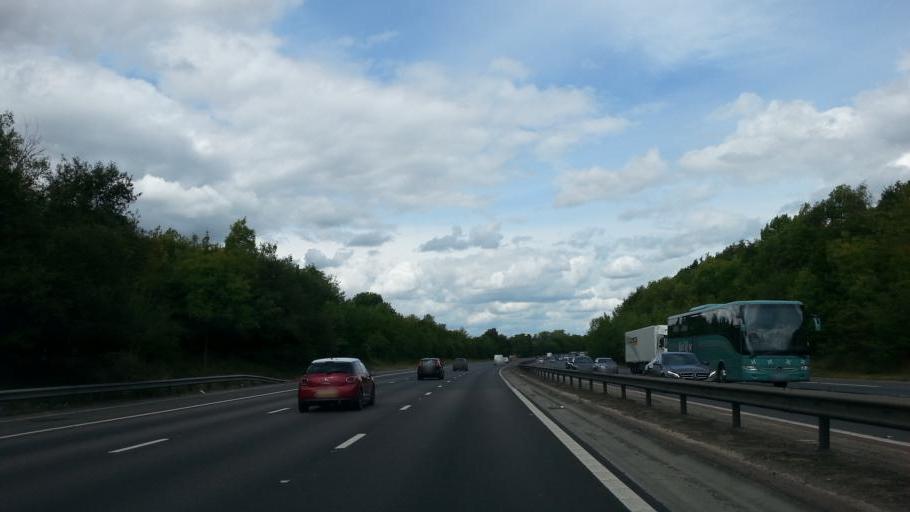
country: GB
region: England
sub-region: Hertfordshire
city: Sawbridgeworth
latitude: 51.8039
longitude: 0.1760
